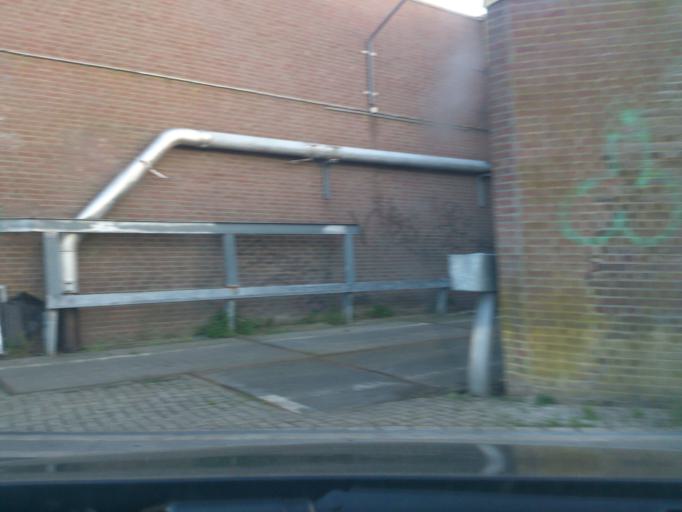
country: NL
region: Gelderland
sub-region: Gemeente Nijmegen
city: Nijmegen
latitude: 51.8527
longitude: 5.8490
